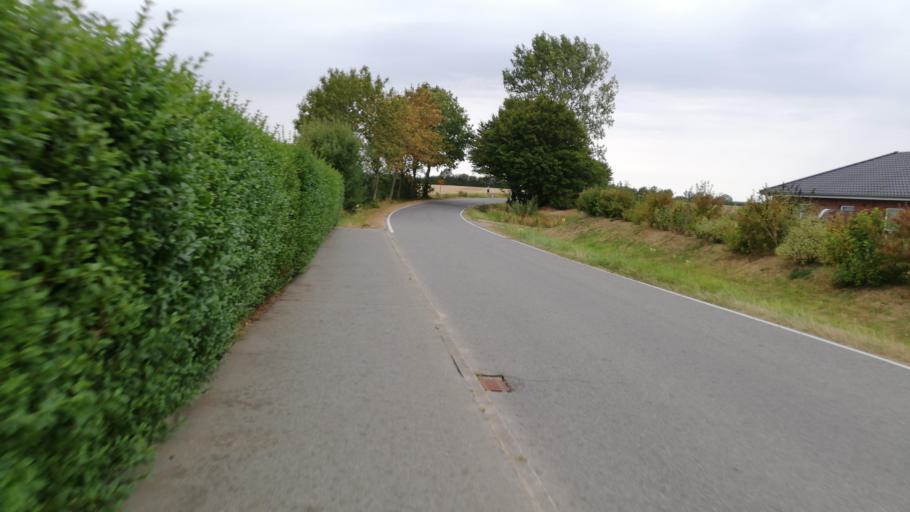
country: DE
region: Schleswig-Holstein
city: Steinbergkirche
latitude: 54.7604
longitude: 9.7619
